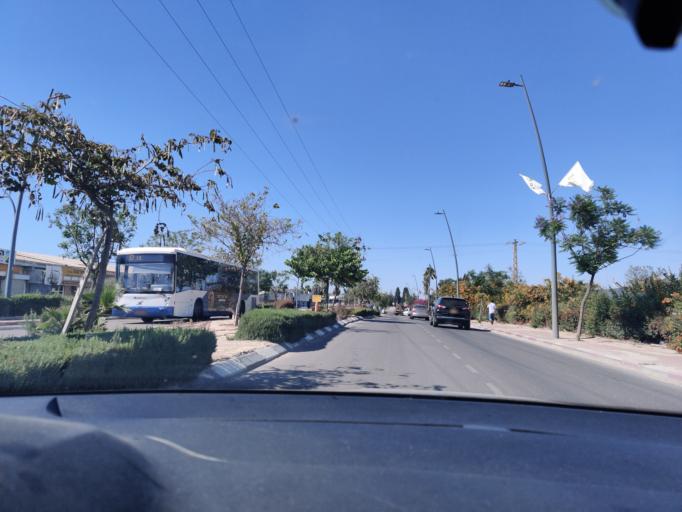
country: IL
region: Southern District
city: Qiryat Gat
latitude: 31.6053
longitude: 34.7848
